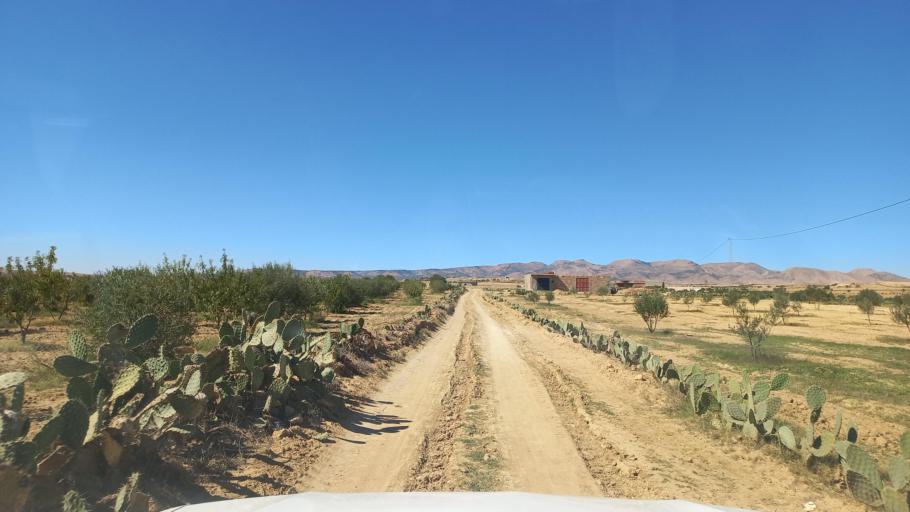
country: TN
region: Al Qasrayn
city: Sbiba
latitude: 35.3662
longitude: 9.0885
